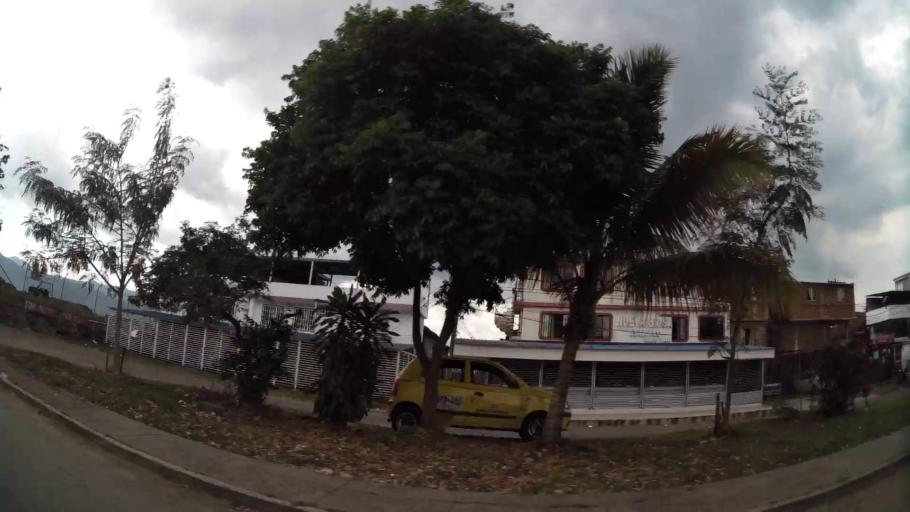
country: CO
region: Valle del Cauca
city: Cali
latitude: 3.4618
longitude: -76.4881
